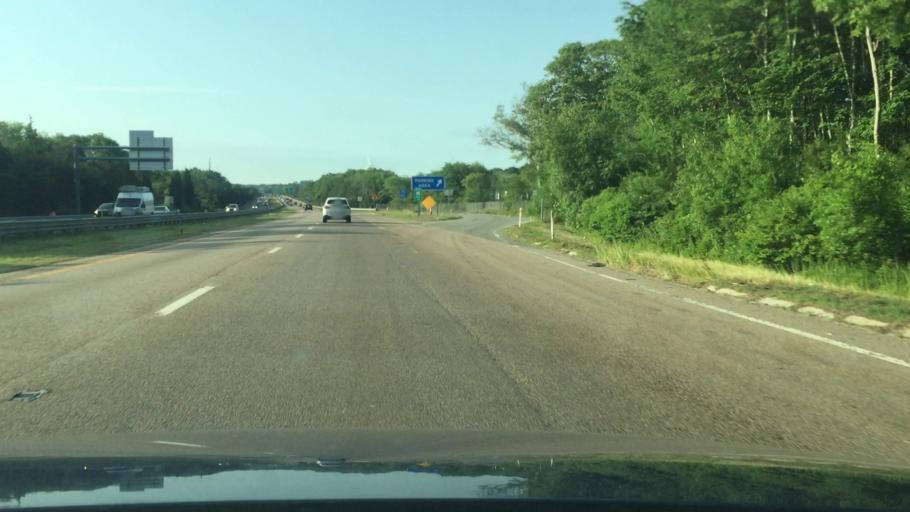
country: US
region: Massachusetts
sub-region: Plymouth County
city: Kingston
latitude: 42.0042
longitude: -70.7250
